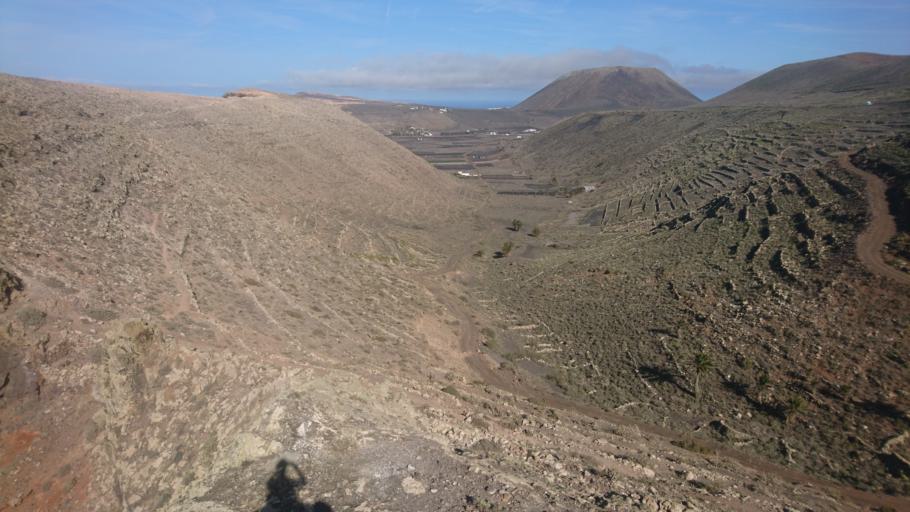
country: ES
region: Canary Islands
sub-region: Provincia de Las Palmas
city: Haria
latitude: 29.1708
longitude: -13.5122
